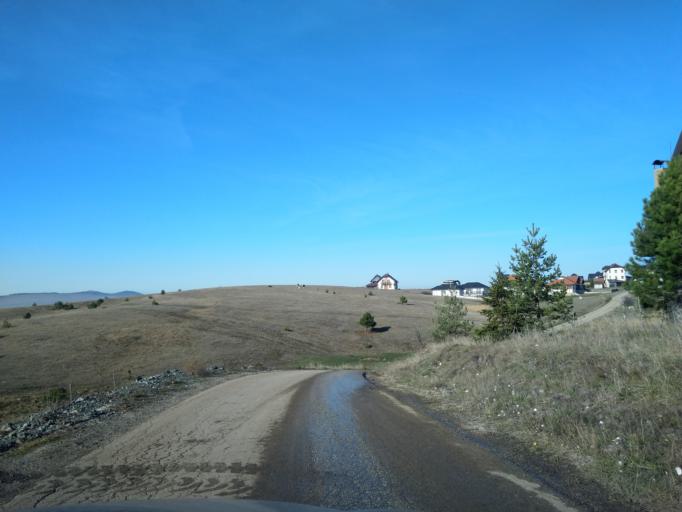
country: RS
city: Zlatibor
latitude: 43.7393
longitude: 19.6757
